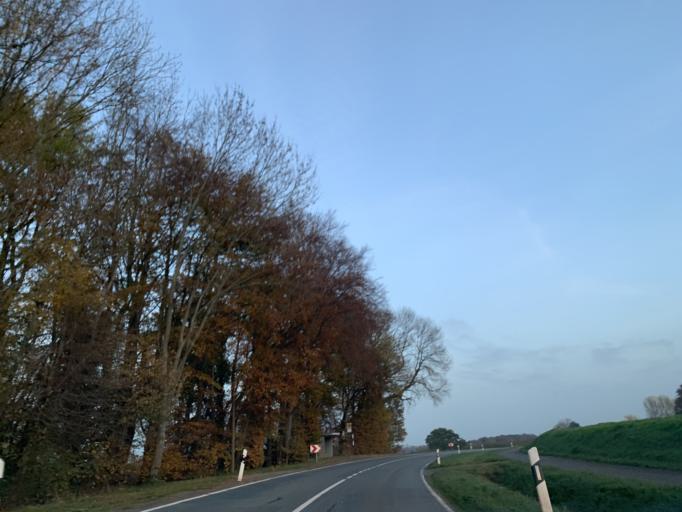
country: DE
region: North Rhine-Westphalia
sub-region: Regierungsbezirk Munster
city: Havixbeck
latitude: 51.9822
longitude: 7.3683
